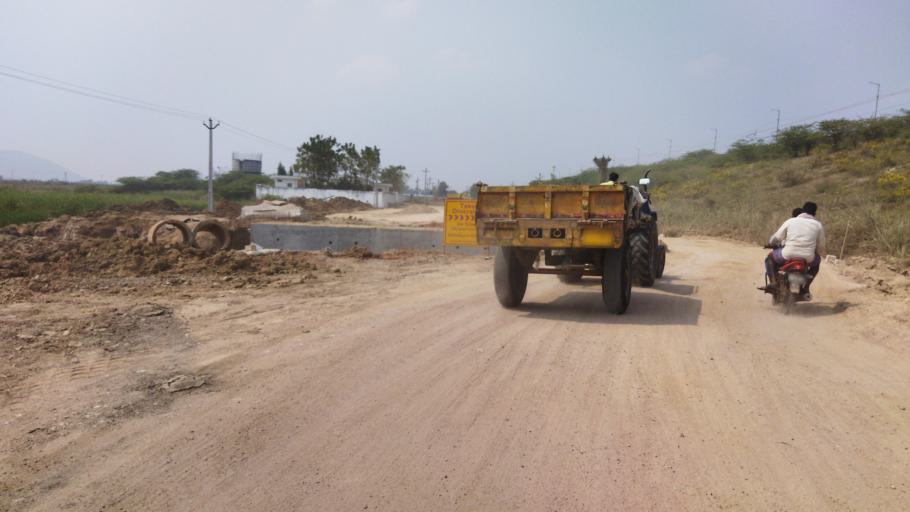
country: IN
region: Telangana
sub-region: Nalgonda
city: Nalgonda
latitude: 17.0793
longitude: 79.3058
